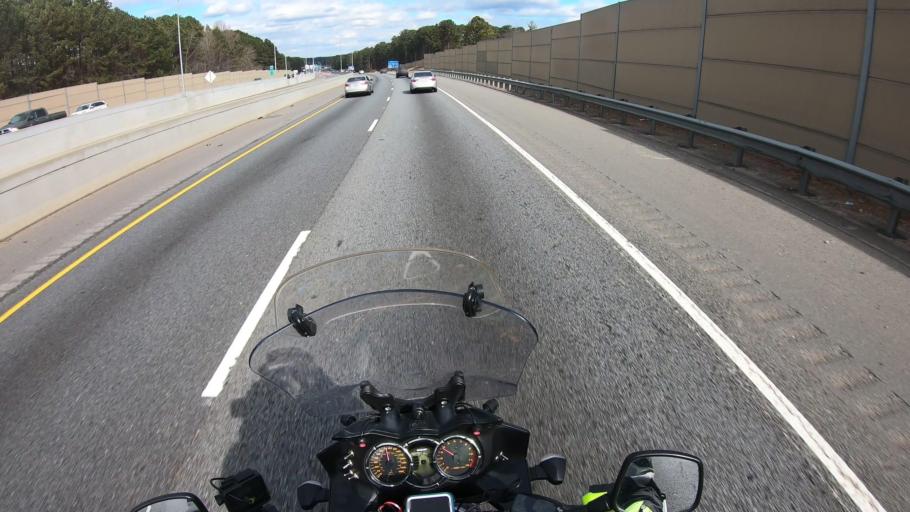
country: US
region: Georgia
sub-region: Cherokee County
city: Woodstock
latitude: 34.0568
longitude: -84.5421
